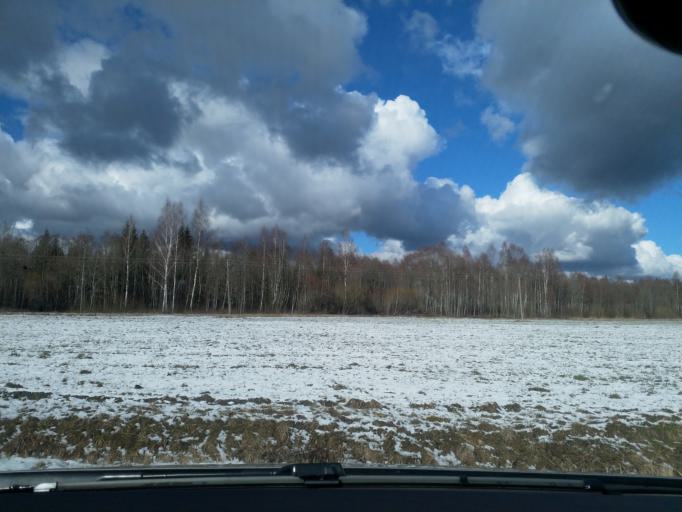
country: LV
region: Talsu Rajons
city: Stende
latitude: 57.0474
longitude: 22.3607
